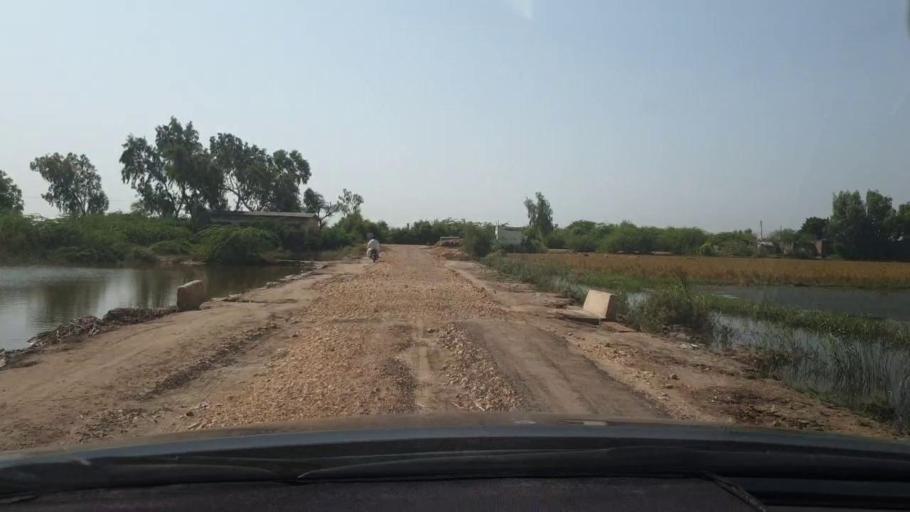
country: PK
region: Sindh
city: Tando Bago
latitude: 24.6987
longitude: 69.1081
